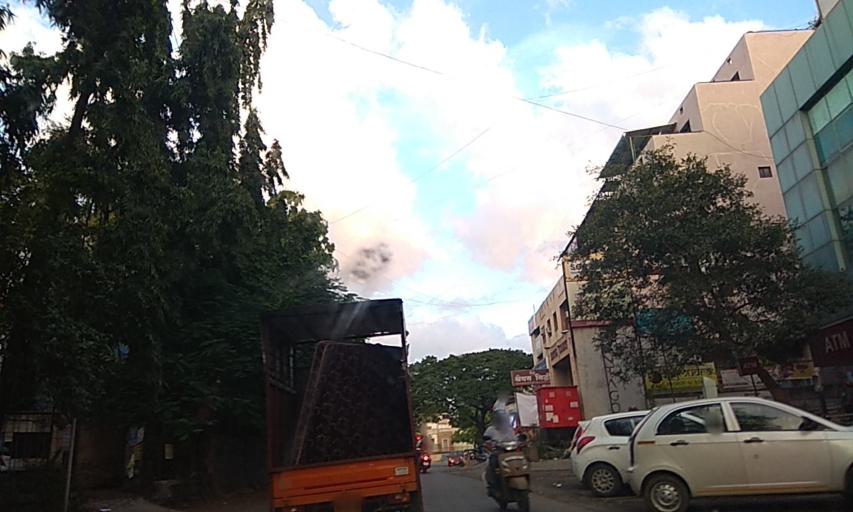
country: IN
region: Maharashtra
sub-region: Pune Division
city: Pune
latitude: 18.4925
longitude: 73.8568
